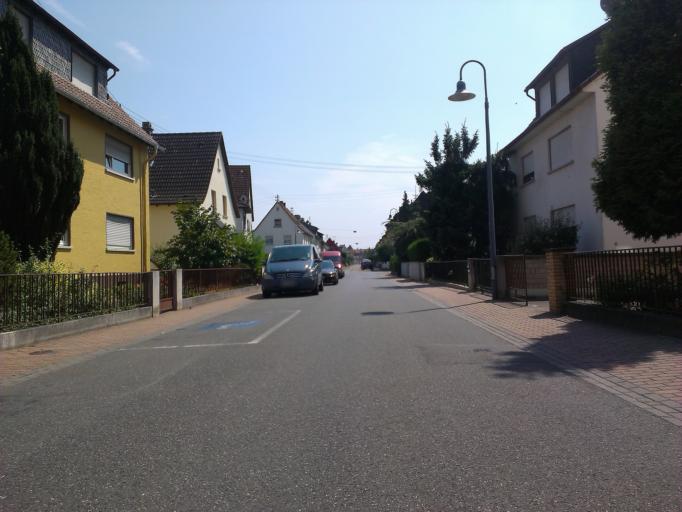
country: DE
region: Baden-Wuerttemberg
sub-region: Karlsruhe Region
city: Edingen-Neckarhausen
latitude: 49.4498
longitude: 8.6057
